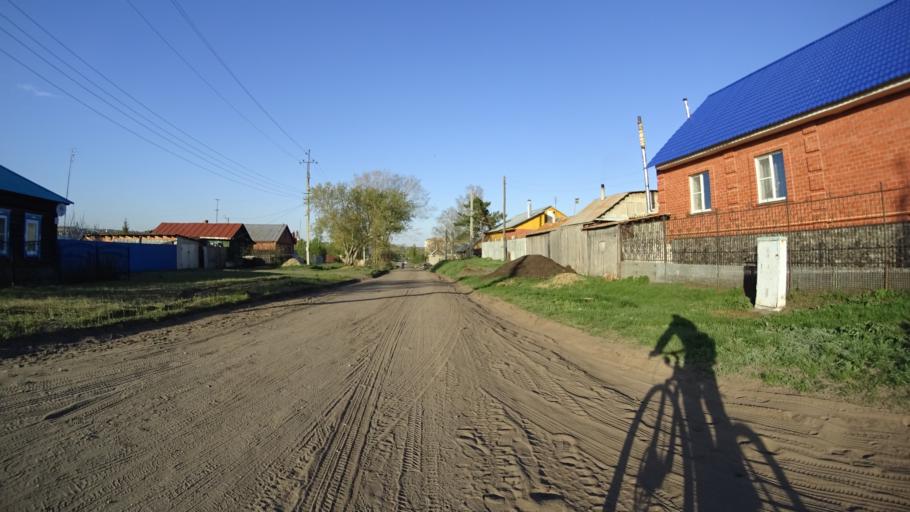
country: RU
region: Chelyabinsk
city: Troitsk
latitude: 54.0876
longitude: 61.5383
